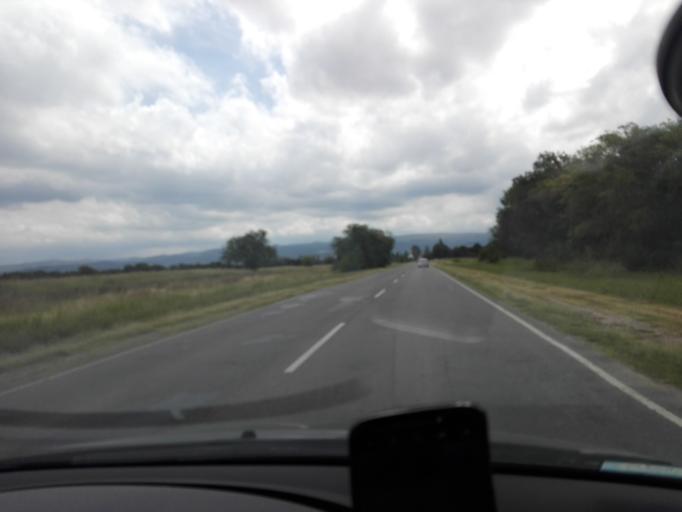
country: AR
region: Cordoba
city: Alta Gracia
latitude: -31.6582
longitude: -64.3922
